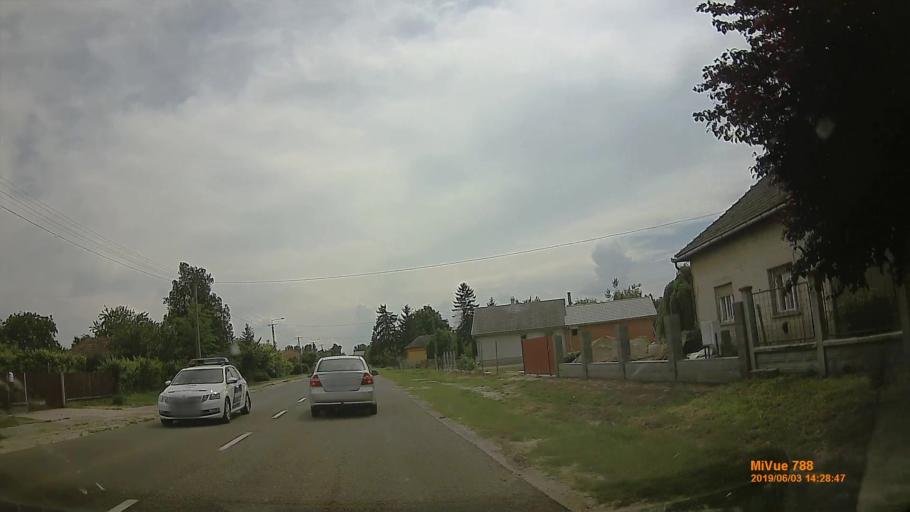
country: HU
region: Bacs-Kiskun
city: Tiszakecske
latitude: 46.9759
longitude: 20.1123
